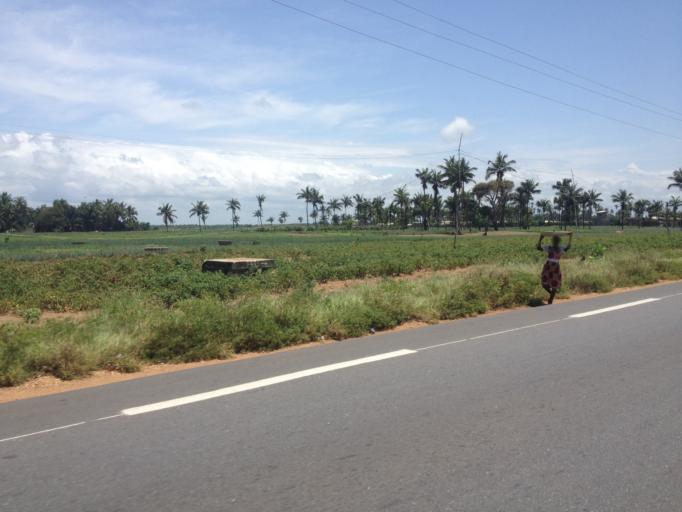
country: BJ
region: Mono
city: Grand-Popo
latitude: 6.2687
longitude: 1.7773
